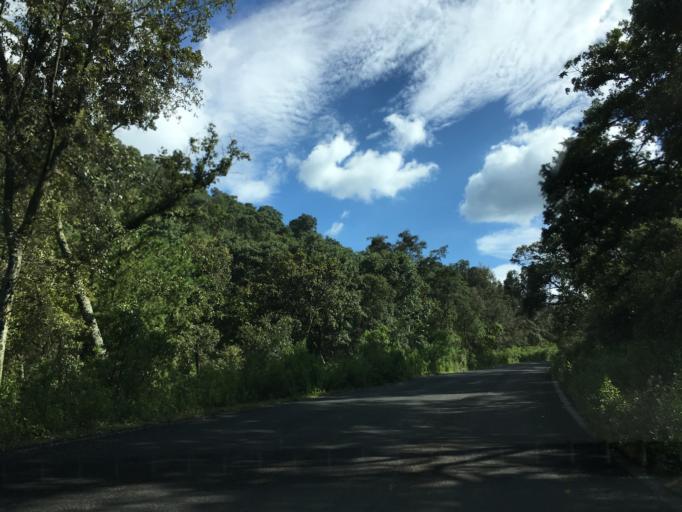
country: MX
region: Michoacan
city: Capula
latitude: 19.7453
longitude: -101.7954
